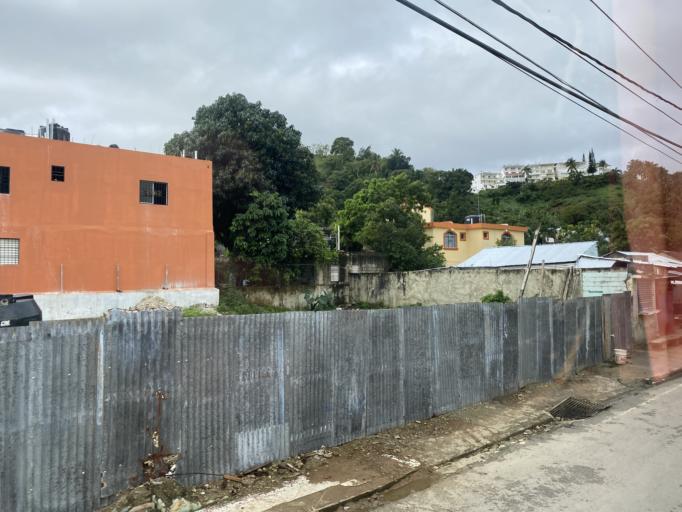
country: DO
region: El Seibo
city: Miches
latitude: 18.9842
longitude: -69.0502
